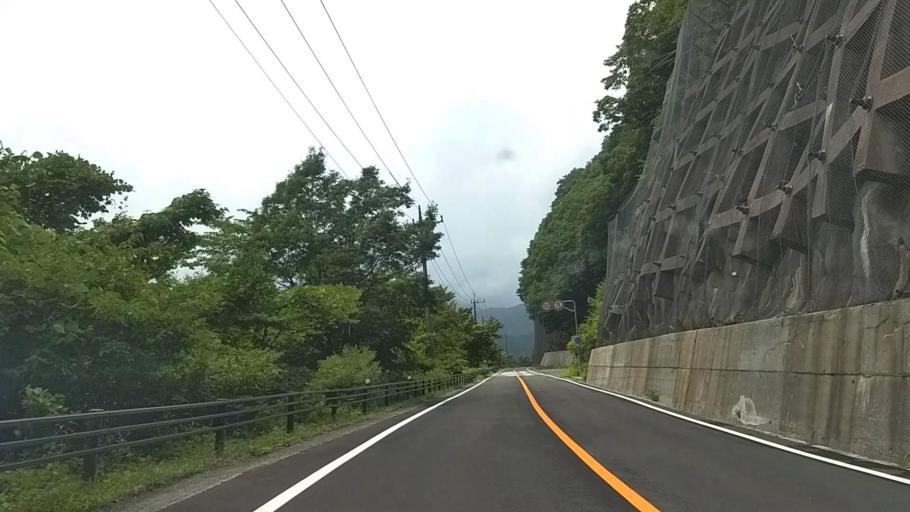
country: JP
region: Yamanashi
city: Fujikawaguchiko
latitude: 35.4754
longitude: 138.5890
